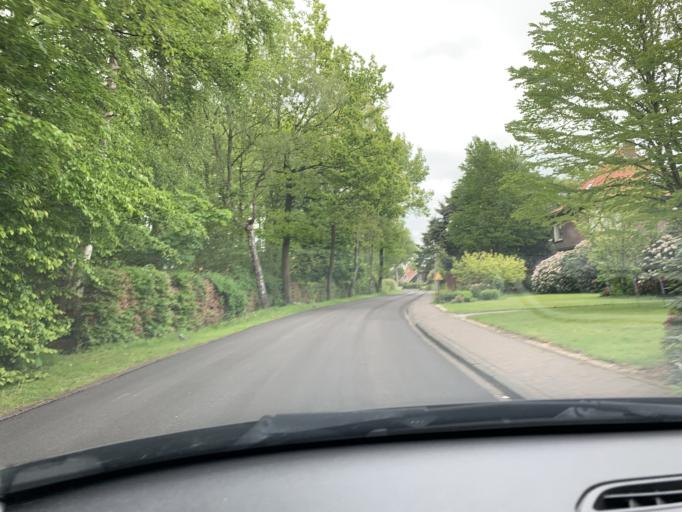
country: DE
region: Lower Saxony
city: Westerstede
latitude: 53.2474
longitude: 7.9133
